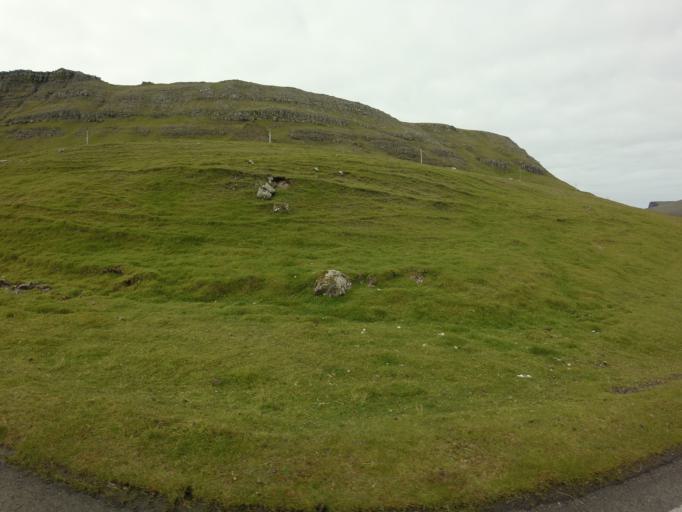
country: FO
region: Suduroy
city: Tvoroyri
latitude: 61.5906
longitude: -6.9469
